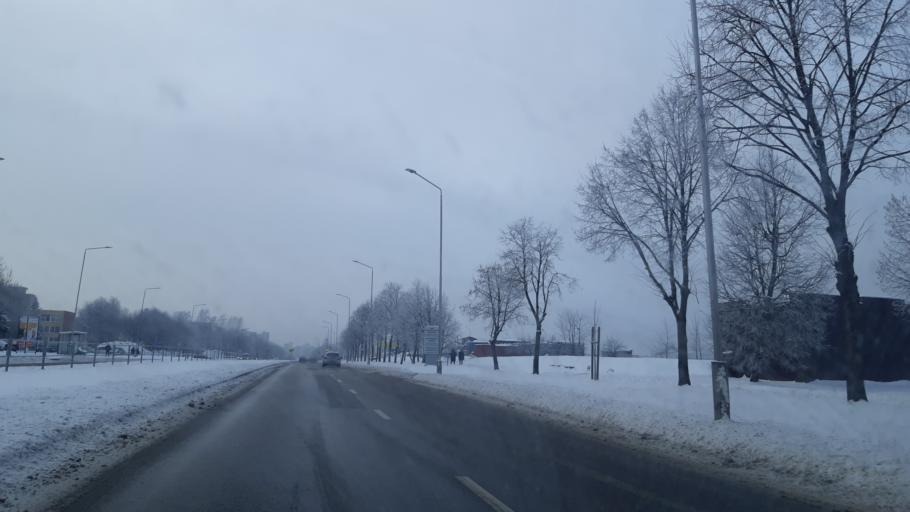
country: LT
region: Kauno apskritis
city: Dainava (Kaunas)
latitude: 54.9310
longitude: 23.9588
